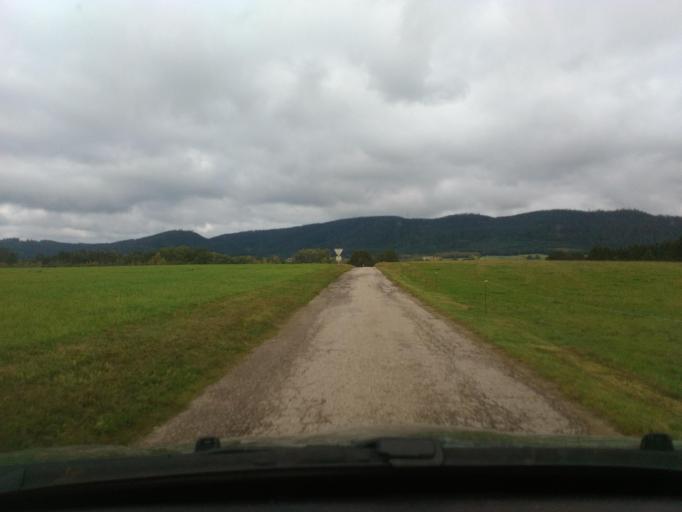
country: FR
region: Lorraine
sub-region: Departement des Vosges
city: Etival-Clairefontaine
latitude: 48.3481
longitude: 6.8599
